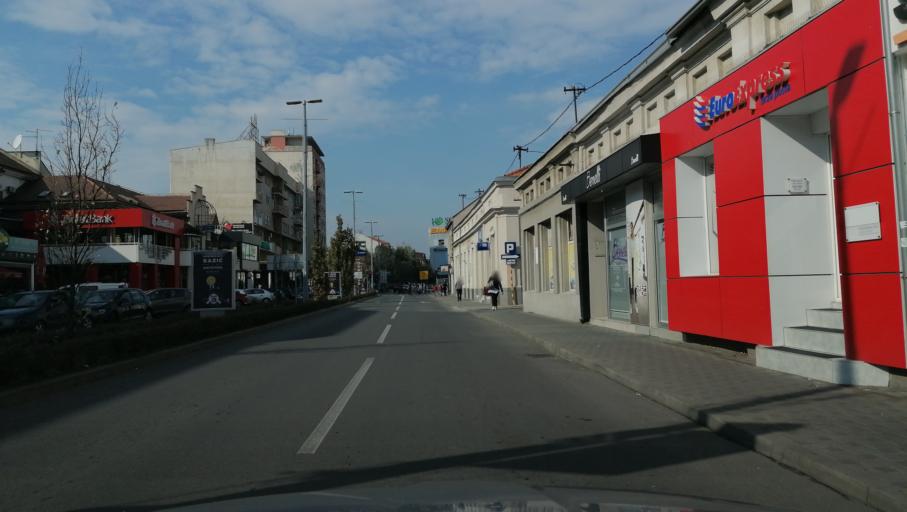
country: BA
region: Republika Srpska
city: Bijeljina
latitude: 44.7550
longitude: 19.2168
